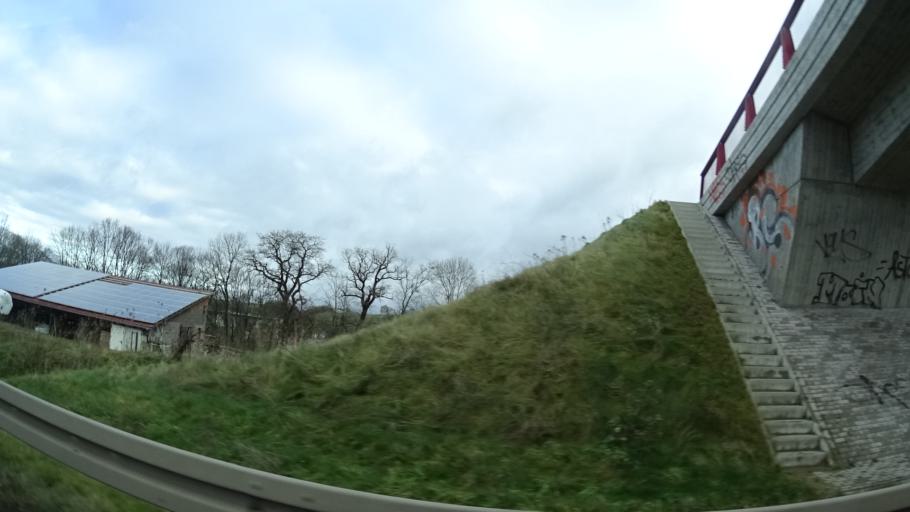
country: DE
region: Thuringia
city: Fambach
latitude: 50.7125
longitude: 10.3703
